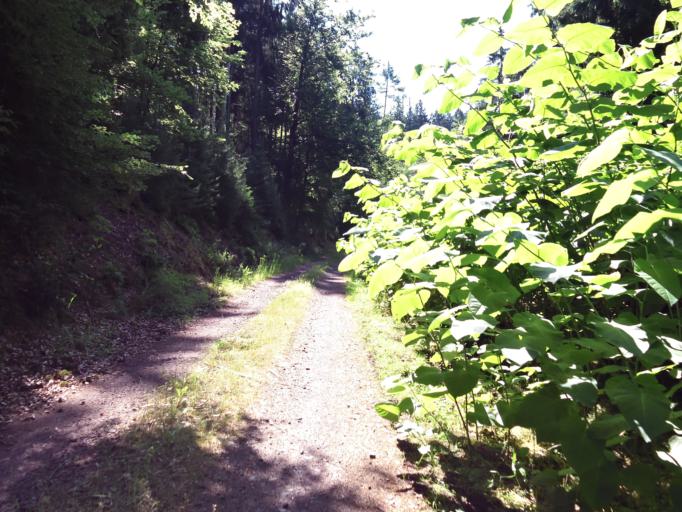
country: DE
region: Rheinland-Pfalz
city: Waldleiningen
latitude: 49.3923
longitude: 7.8637
